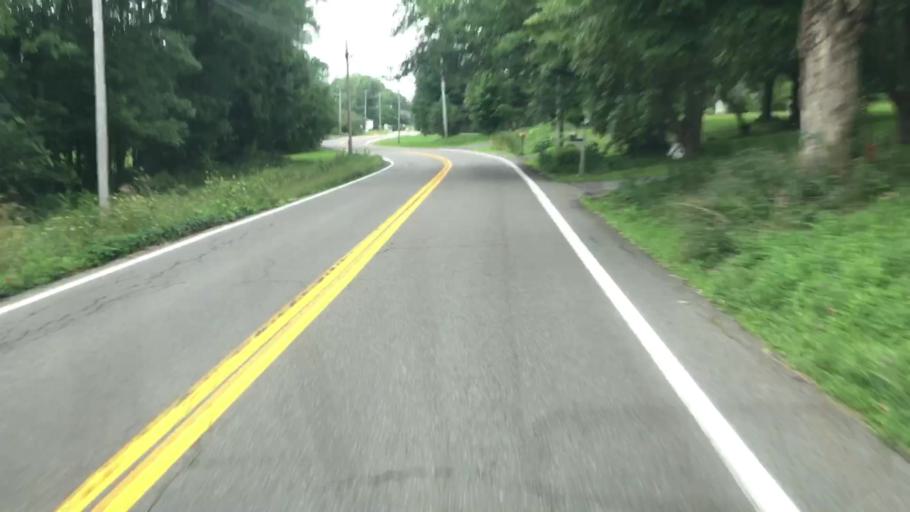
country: US
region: New York
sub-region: Onondaga County
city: Skaneateles
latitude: 42.9847
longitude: -76.4497
